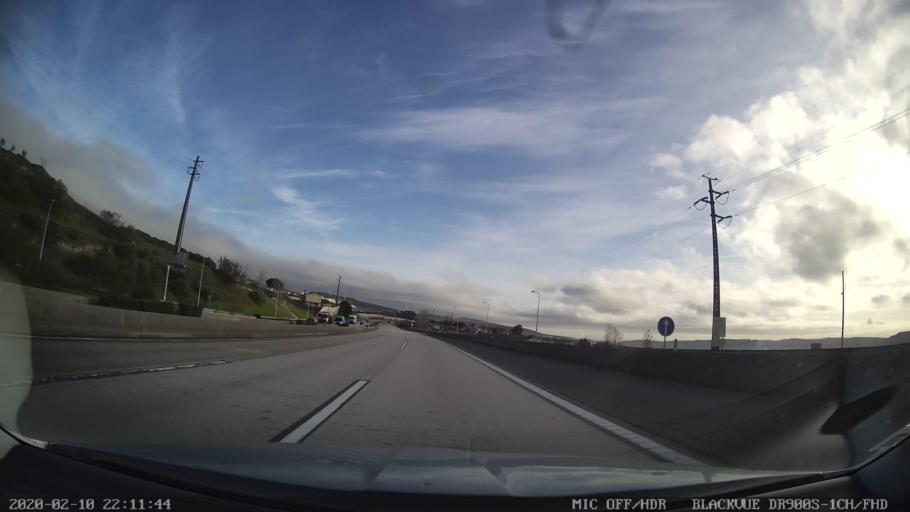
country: PT
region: Lisbon
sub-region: Loures
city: Loures
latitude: 38.8528
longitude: -9.1729
